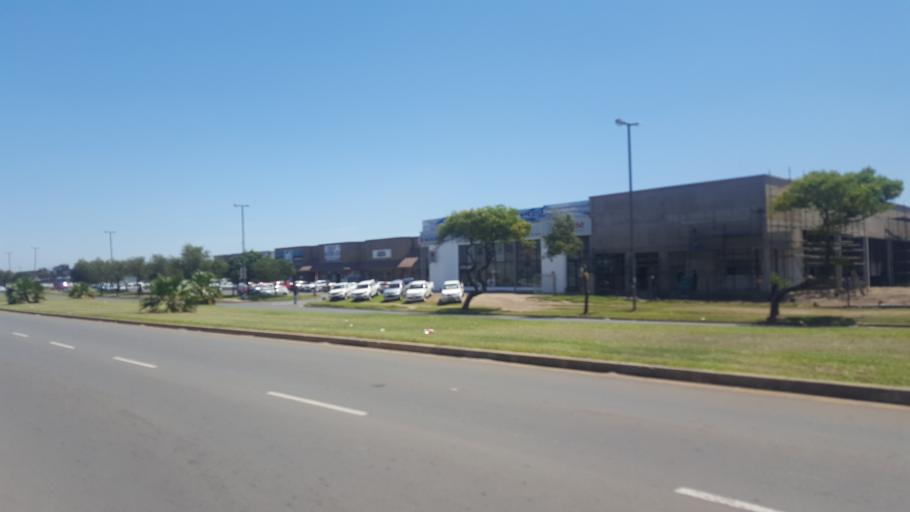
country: ZA
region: KwaZulu-Natal
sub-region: uThungulu District Municipality
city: Richards Bay
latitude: -28.7450
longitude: 32.0510
